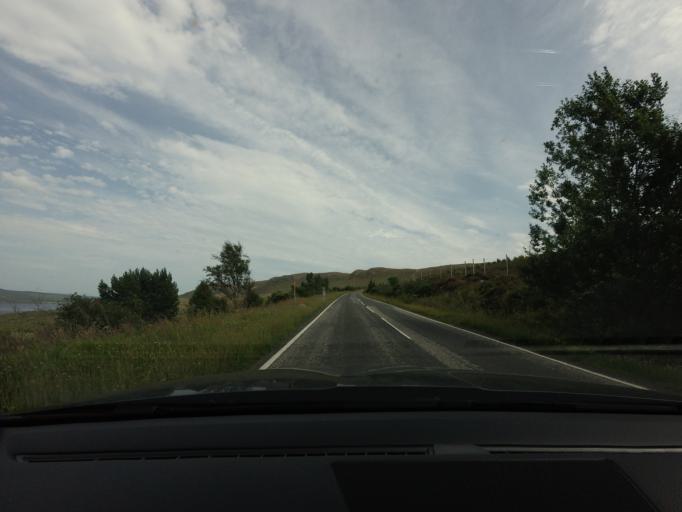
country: GB
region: Scotland
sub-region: Highland
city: Alness
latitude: 57.8428
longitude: -4.2814
